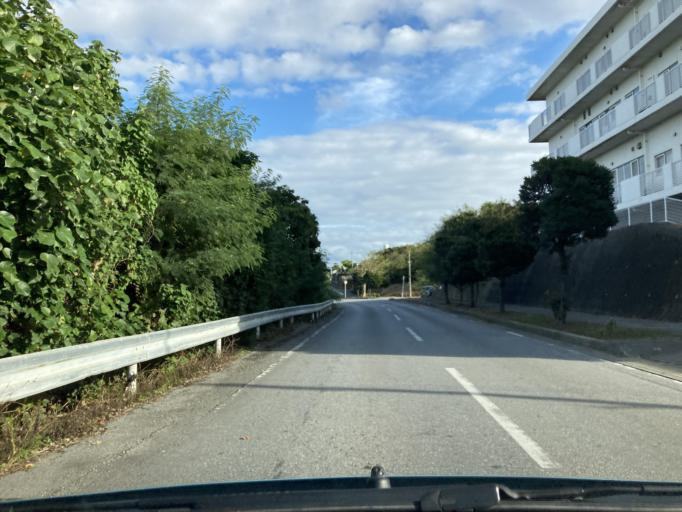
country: JP
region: Okinawa
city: Itoman
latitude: 26.1323
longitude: 127.7546
